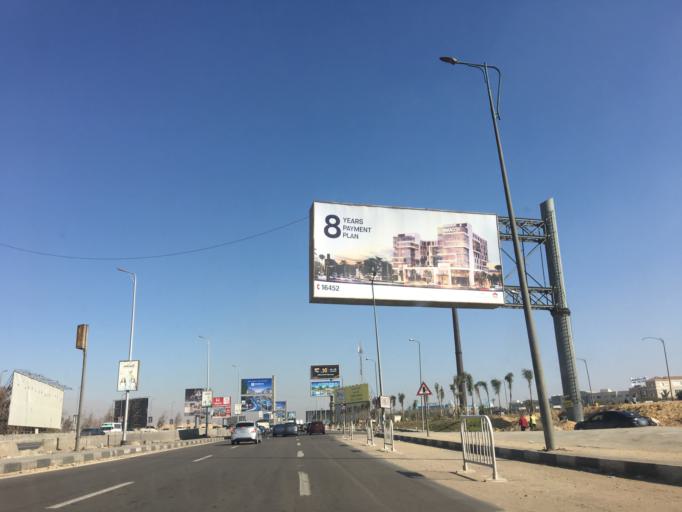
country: EG
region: Muhafazat al Qalyubiyah
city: Al Khankah
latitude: 30.0555
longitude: 31.4129
